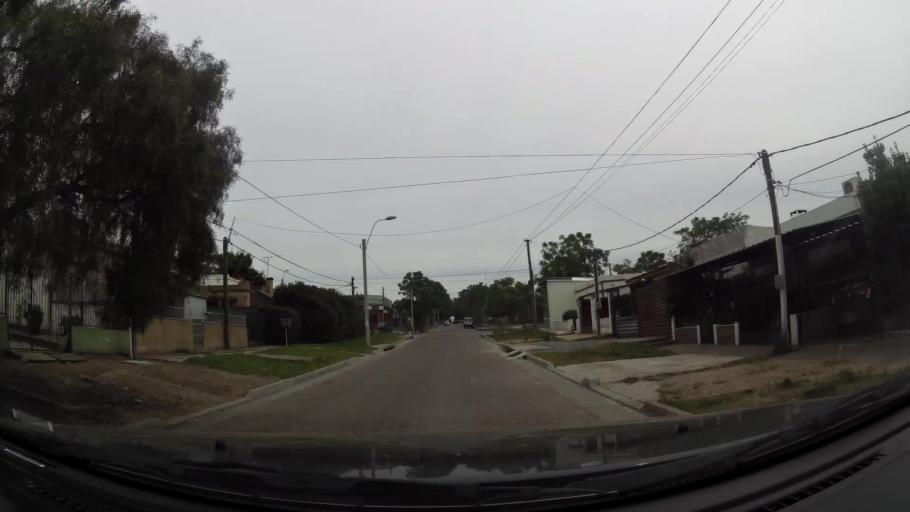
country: UY
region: Canelones
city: La Paz
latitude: -34.7651
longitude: -56.2289
